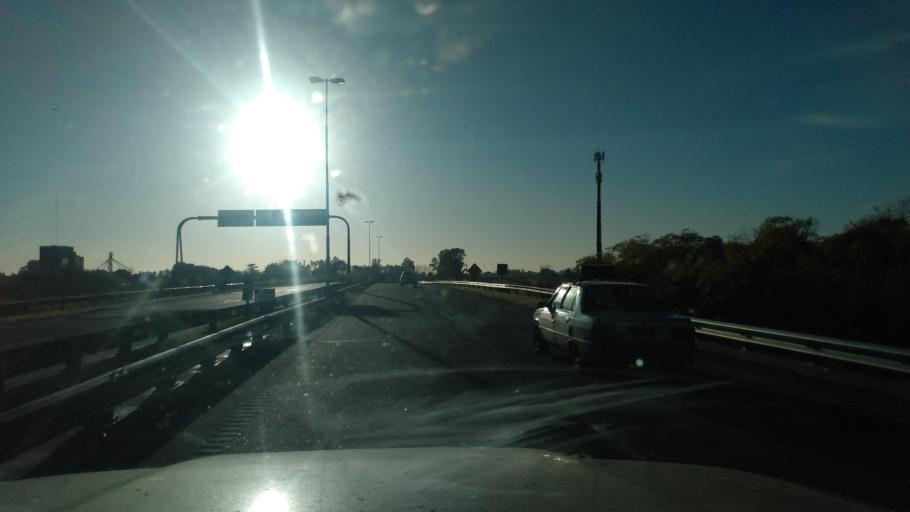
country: AR
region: Buenos Aires
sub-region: Partido de Lujan
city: Lujan
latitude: -34.5460
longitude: -59.1632
